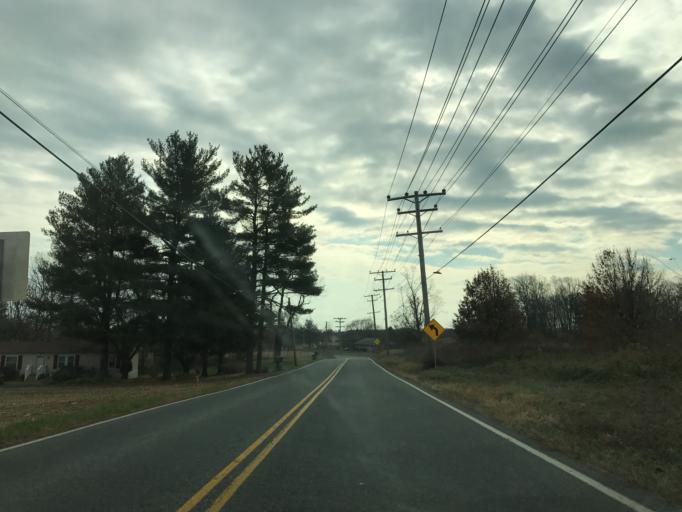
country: US
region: Maryland
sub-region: Harford County
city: Jarrettsville
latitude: 39.5846
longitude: -76.4289
